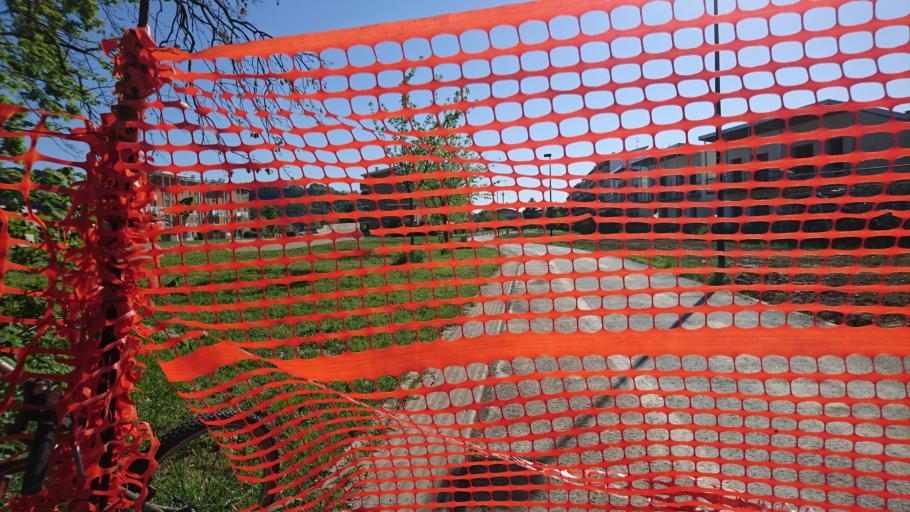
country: IT
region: The Marches
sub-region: Provincia di Pesaro e Urbino
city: Pesaro
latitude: 43.8889
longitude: 12.8770
